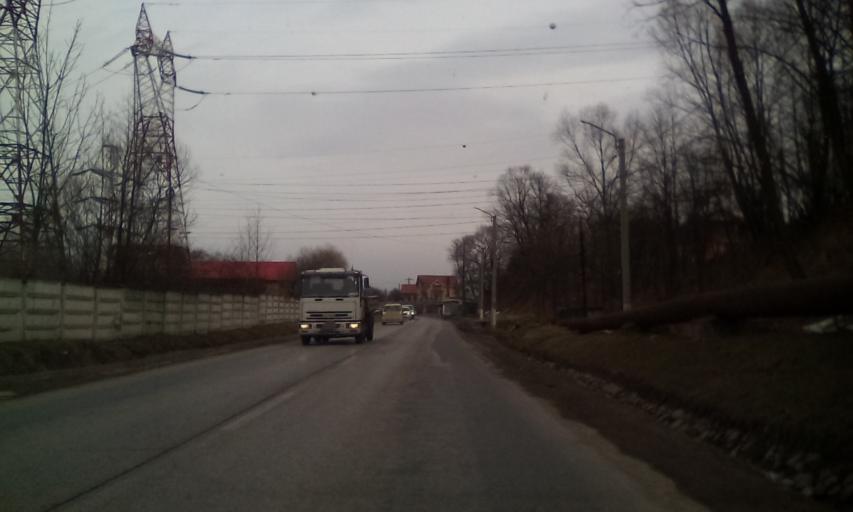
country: RO
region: Hunedoara
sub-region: Municipiul  Vulcan
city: Jiu-Paroseni
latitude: 45.3646
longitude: 23.2656
